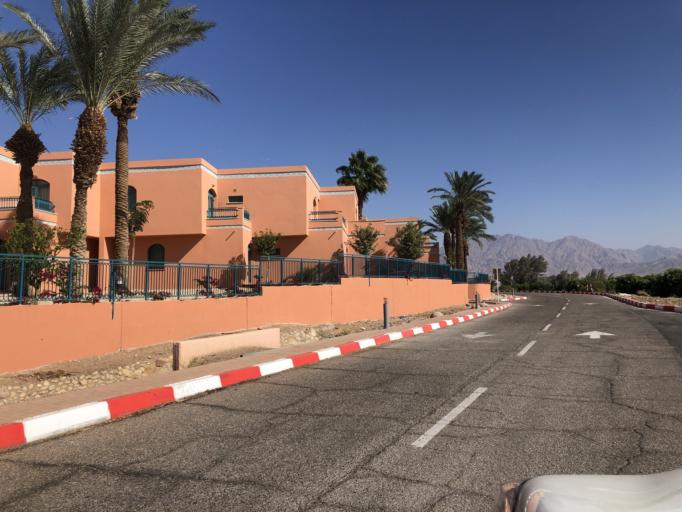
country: IL
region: Southern District
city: Eilat
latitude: 29.5792
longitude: 34.9620
